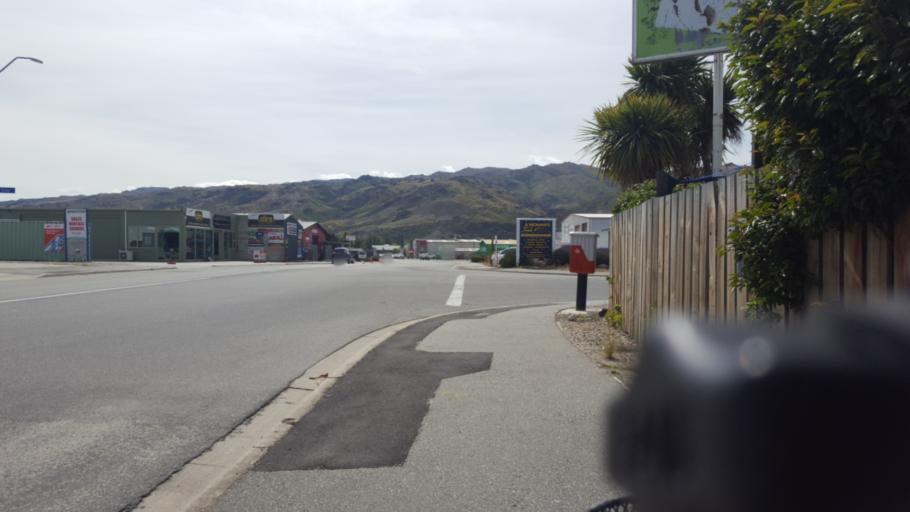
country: NZ
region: Otago
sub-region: Queenstown-Lakes District
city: Wanaka
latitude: -45.0498
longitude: 169.1913
